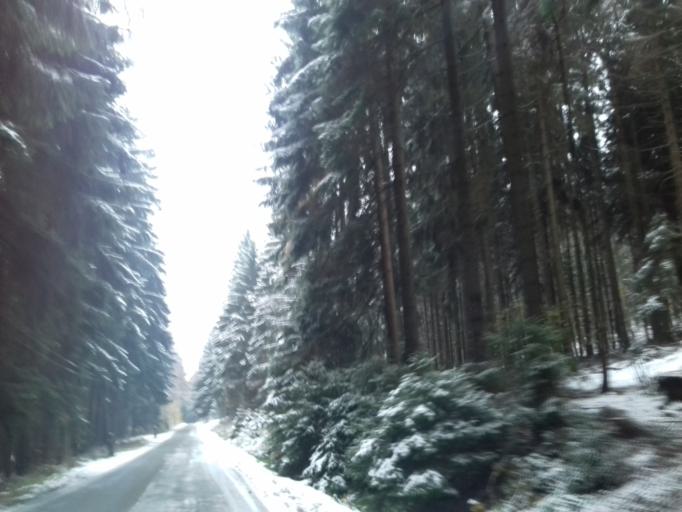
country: CZ
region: Plzensky
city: Postrekov
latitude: 49.4401
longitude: 12.7863
